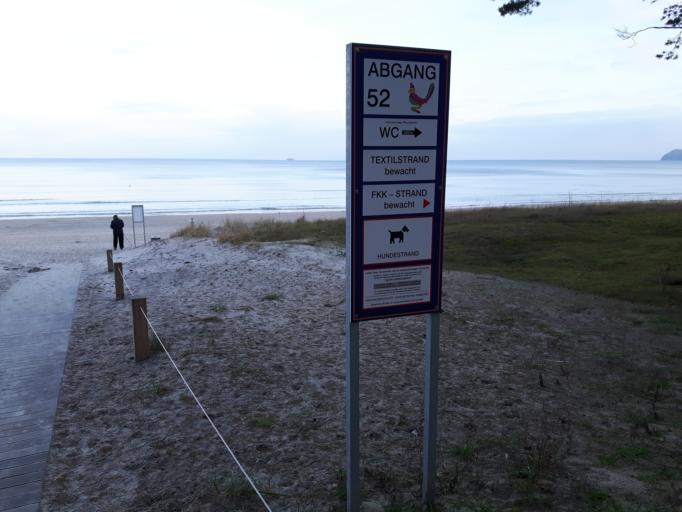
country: DE
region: Mecklenburg-Vorpommern
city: Ostseebad Binz
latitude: 54.4194
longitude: 13.5922
